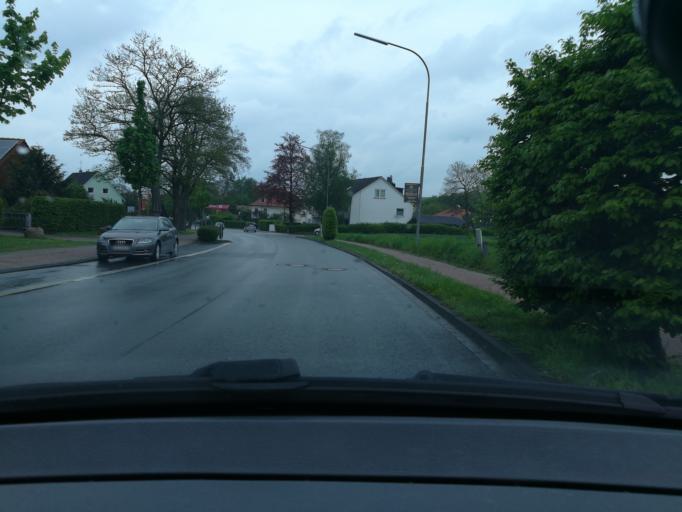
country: DE
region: North Rhine-Westphalia
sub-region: Regierungsbezirk Detmold
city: Herford
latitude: 52.1011
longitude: 8.6824
